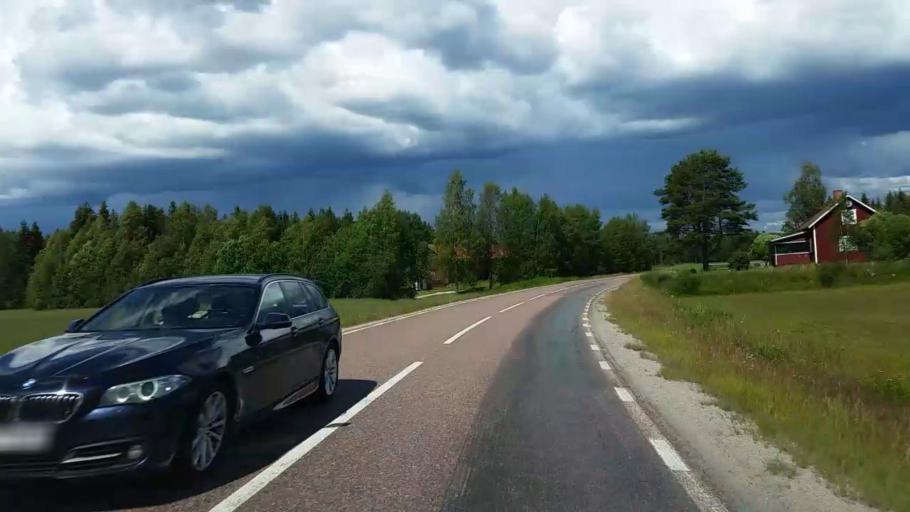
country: SE
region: Gaevleborg
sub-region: Ovanakers Kommun
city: Edsbyn
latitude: 61.3378
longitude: 15.5424
